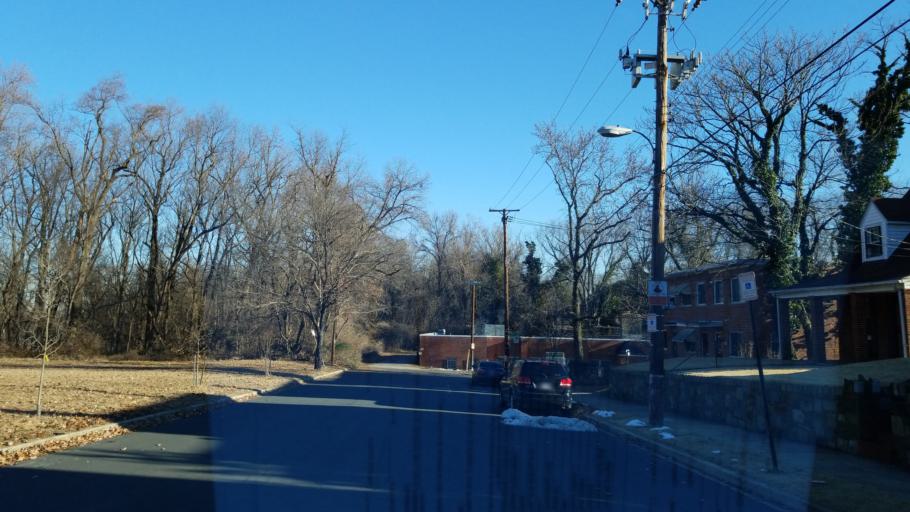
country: US
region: Maryland
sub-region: Prince George's County
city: Glassmanor
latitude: 38.8341
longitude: -77.0104
